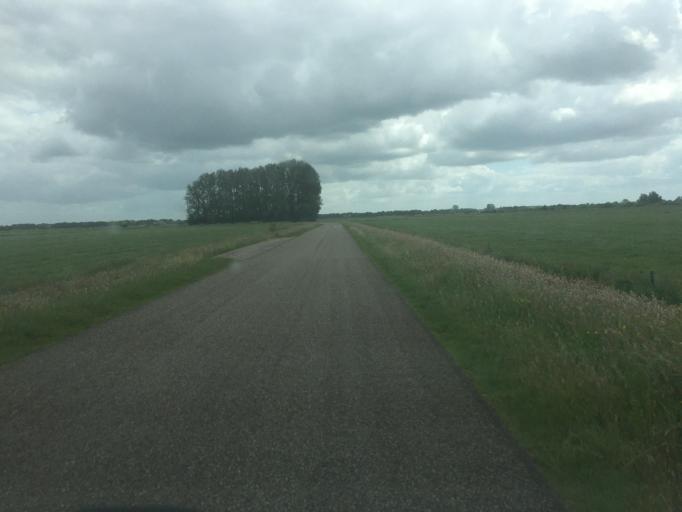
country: NL
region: Friesland
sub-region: Gemeente Heerenveen
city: Nieuwehorne
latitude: 52.9244
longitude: 6.0333
